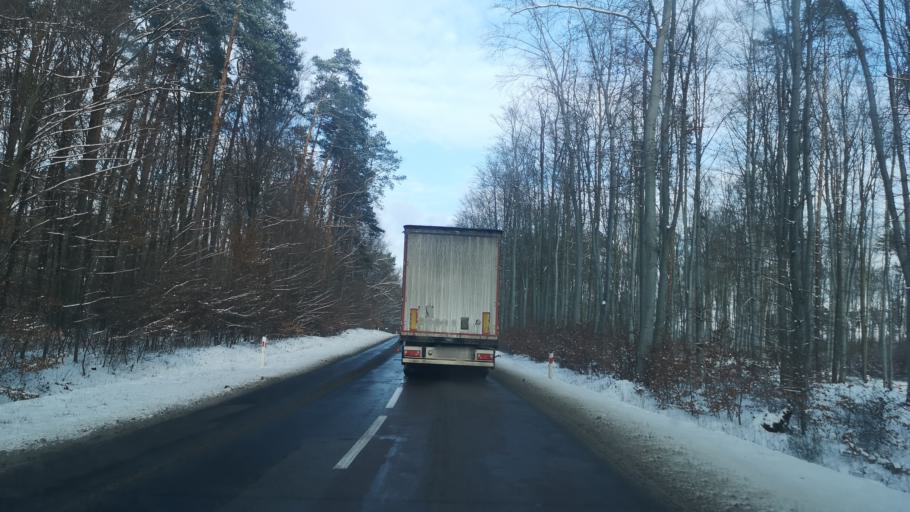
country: PL
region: Subcarpathian Voivodeship
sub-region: Powiat przeworski
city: Sieniawa
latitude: 50.2109
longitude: 22.6433
